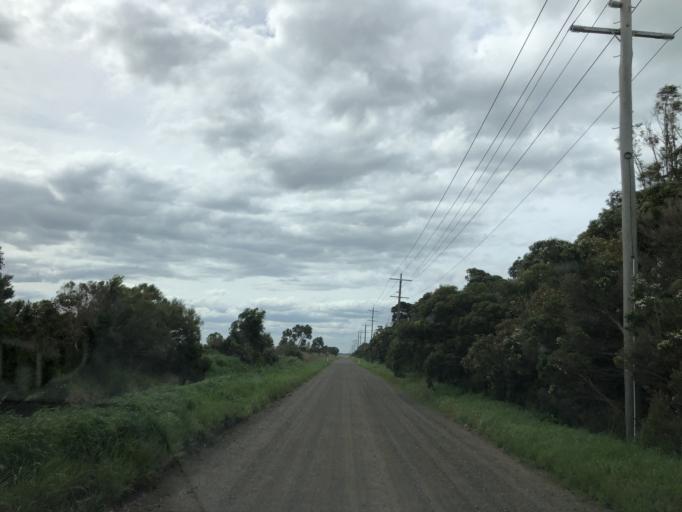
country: AU
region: Victoria
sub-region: Frankston
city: Carrum Downs
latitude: -38.0814
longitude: 145.1646
